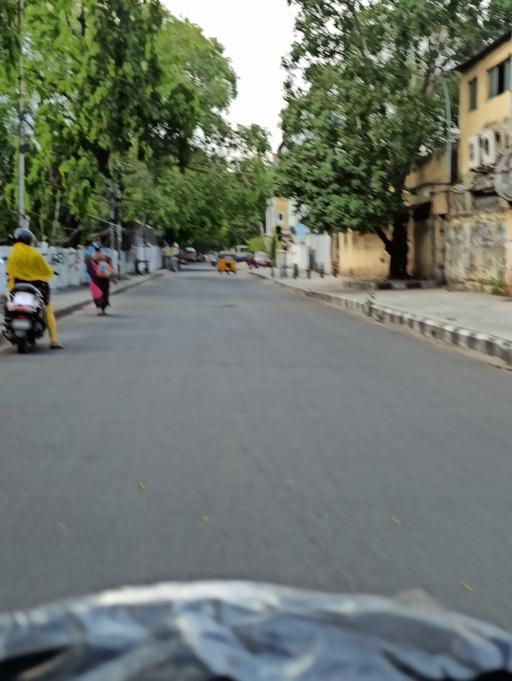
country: IN
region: Tamil Nadu
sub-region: Chennai
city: Chetput
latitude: 13.0491
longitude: 80.2075
